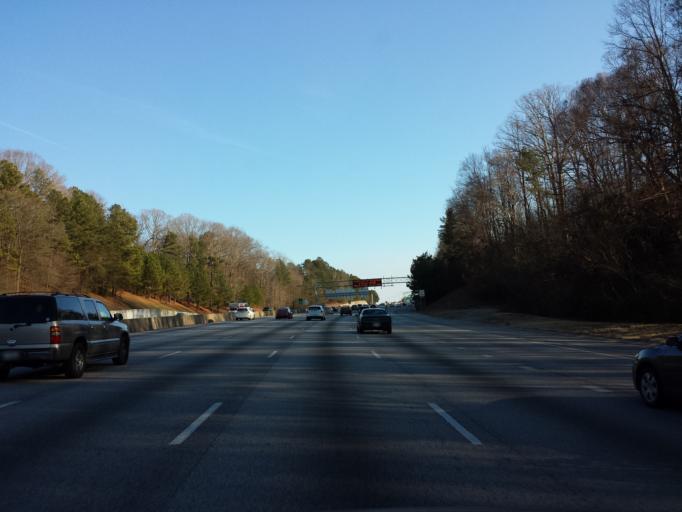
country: US
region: Georgia
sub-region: Cobb County
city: Vinings
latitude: 33.8727
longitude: -84.4451
